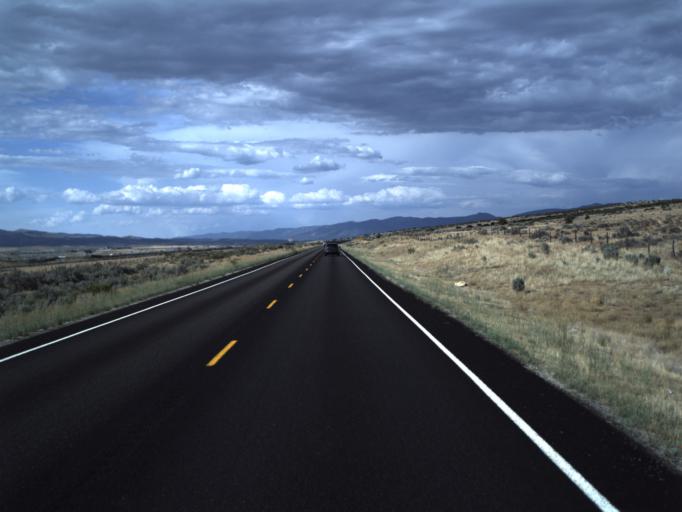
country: US
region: Utah
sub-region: Sanpete County
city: Ephraim
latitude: 39.4339
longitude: -111.5527
